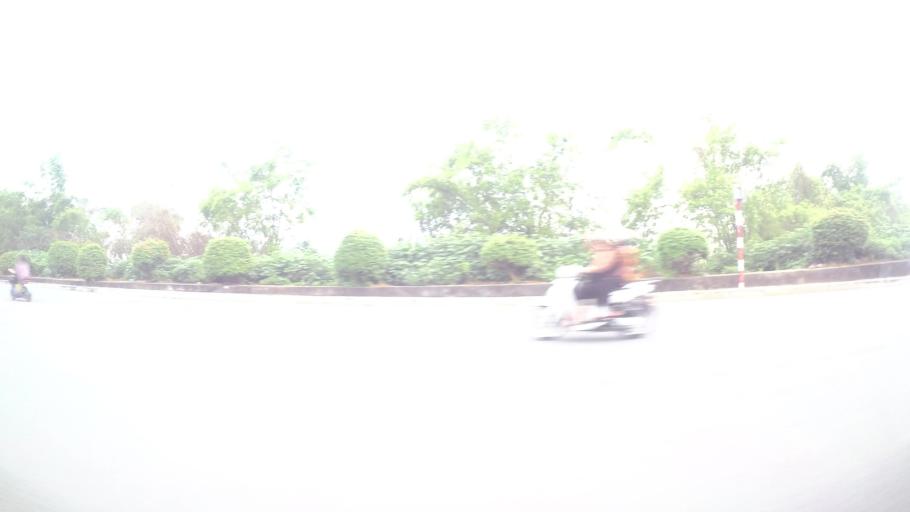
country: VN
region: Ha Noi
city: Hoan Kiem
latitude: 21.0770
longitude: 105.8992
